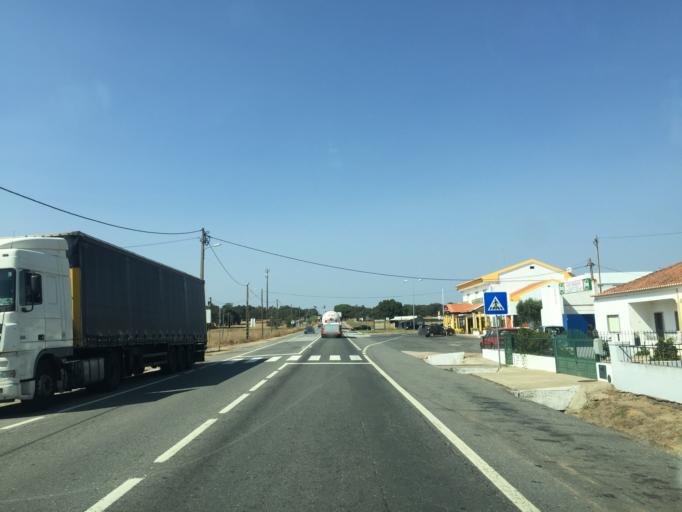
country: PT
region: Beja
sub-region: Aljustrel
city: Aljustrel
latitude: 37.9481
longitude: -8.3807
